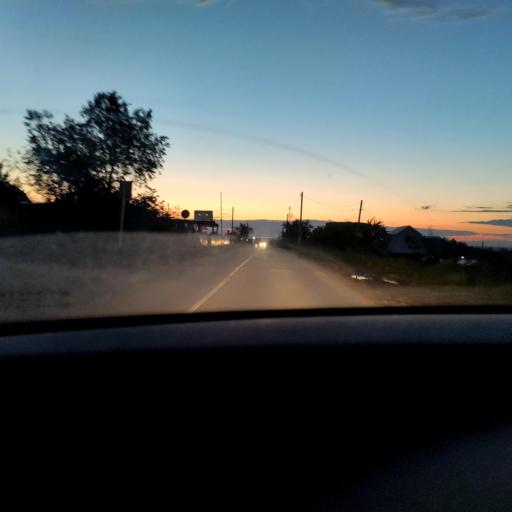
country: RU
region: Samara
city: Novosemeykino
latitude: 53.3996
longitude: 50.3241
